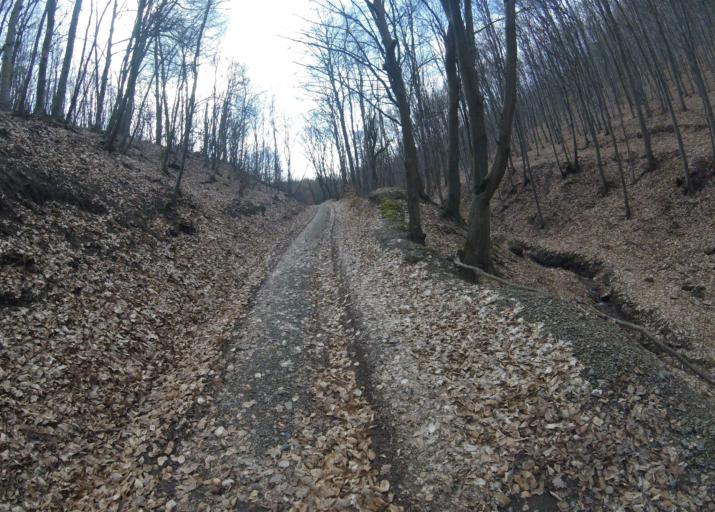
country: HU
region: Heves
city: Belapatfalva
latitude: 48.0344
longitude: 20.3539
